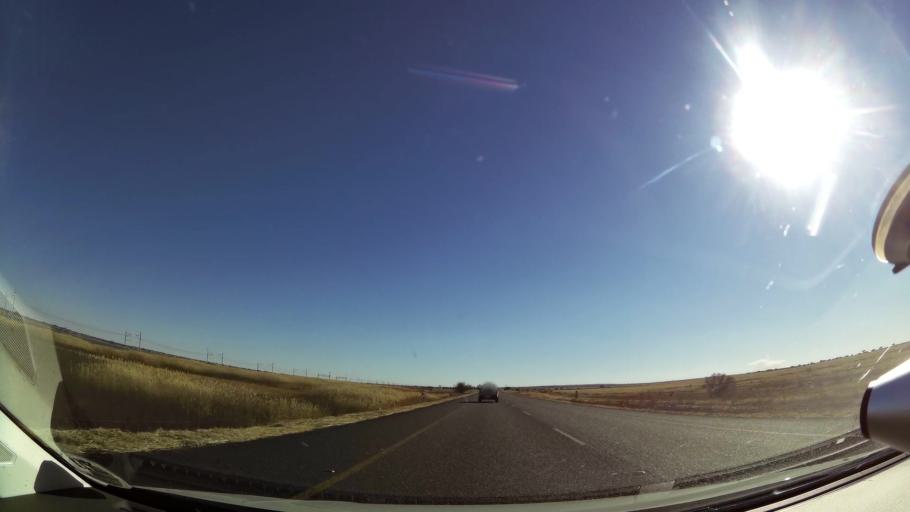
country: ZA
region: Northern Cape
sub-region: Frances Baard District Municipality
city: Kimberley
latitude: -28.6768
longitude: 24.7774
